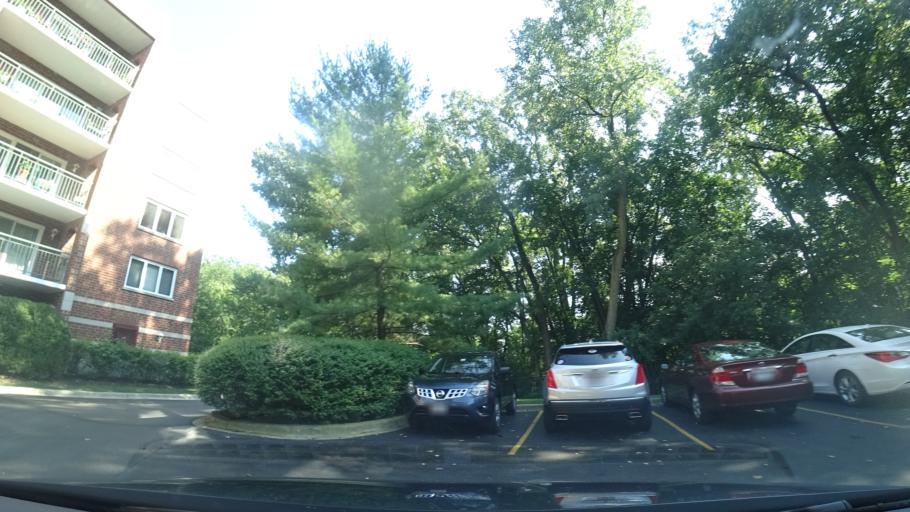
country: US
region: Illinois
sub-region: Cook County
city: Lincolnwood
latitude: 41.9778
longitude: -87.7376
